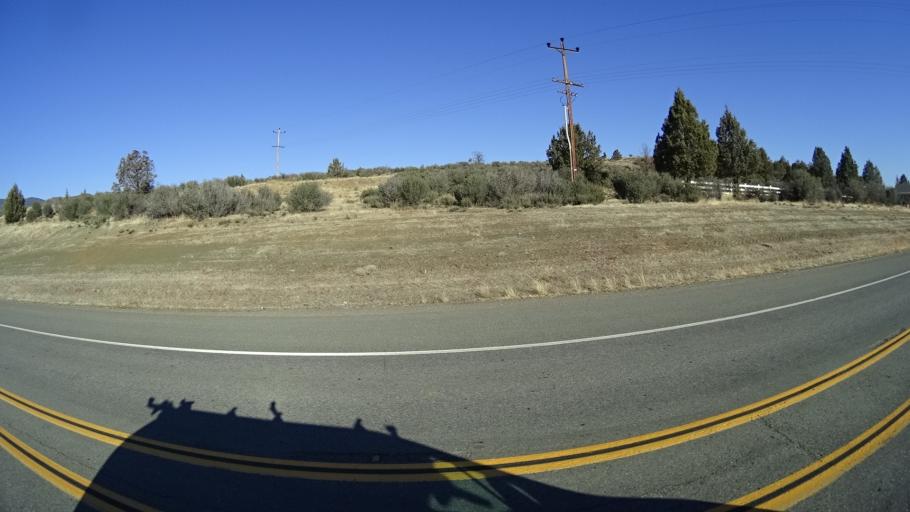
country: US
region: California
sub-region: Siskiyou County
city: Yreka
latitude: 41.7391
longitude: -122.6167
